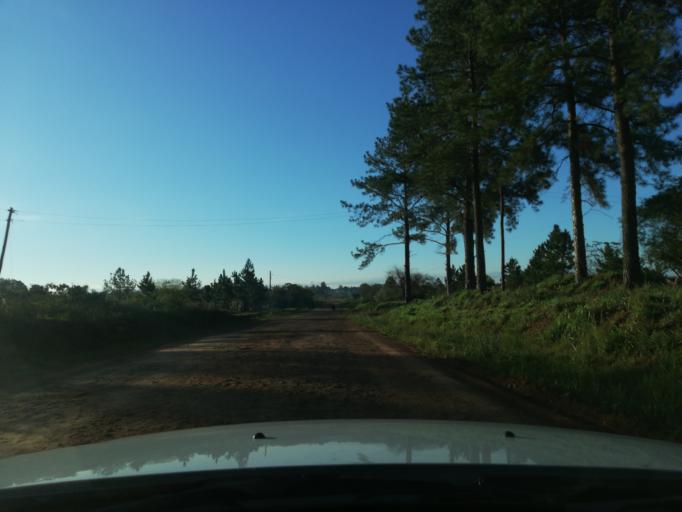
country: AR
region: Misiones
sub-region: Departamento de Capital
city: Posadas
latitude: -27.4763
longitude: -55.9708
